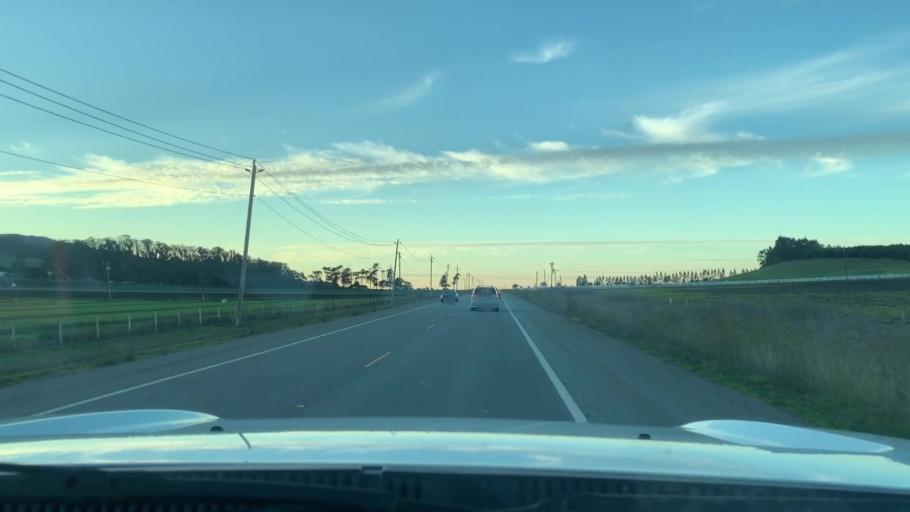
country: US
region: California
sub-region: San Luis Obispo County
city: San Luis Obispo
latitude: 35.2837
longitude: -120.7305
